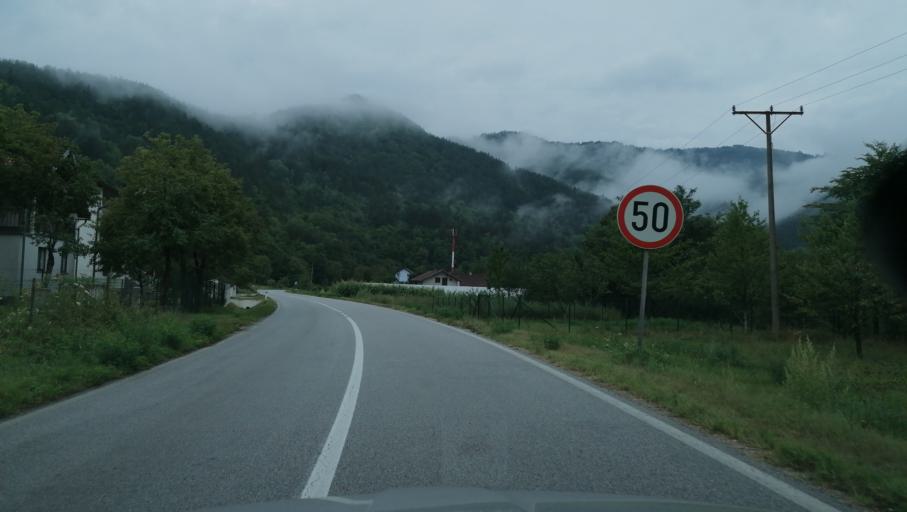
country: RS
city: Durici
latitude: 43.7565
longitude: 19.3940
